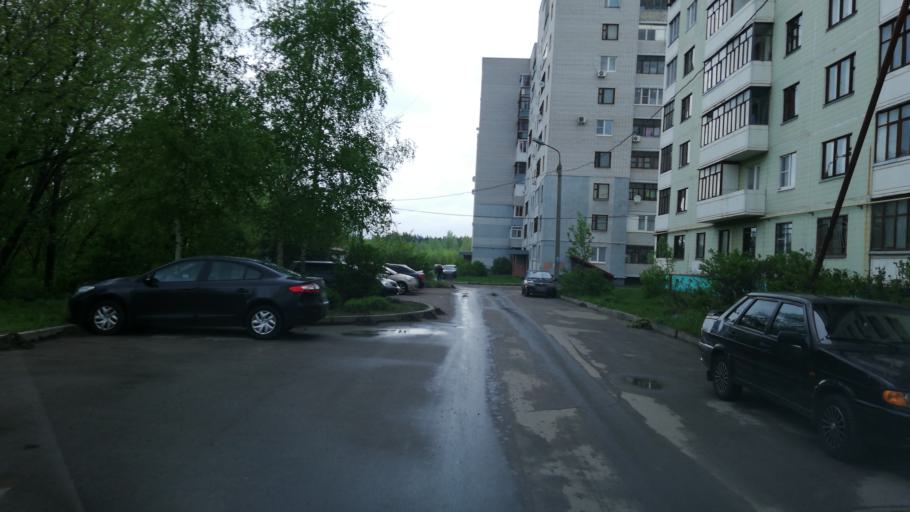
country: RU
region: Jaroslavl
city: Yaroslavl
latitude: 57.6574
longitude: 39.9244
